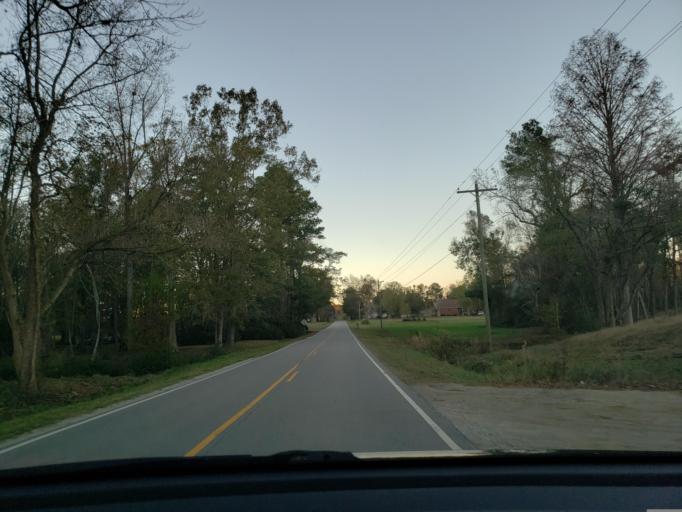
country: US
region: North Carolina
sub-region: Onslow County
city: Jacksonville
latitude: 34.7265
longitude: -77.5815
